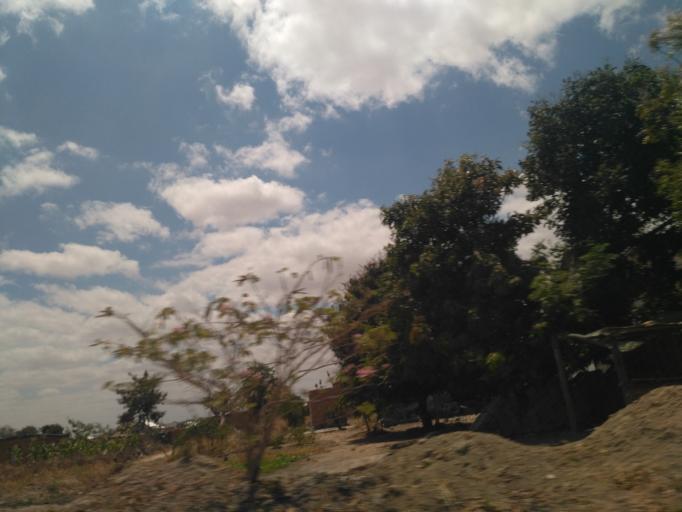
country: TZ
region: Dodoma
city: Kisasa
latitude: -6.1661
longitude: 35.7983
